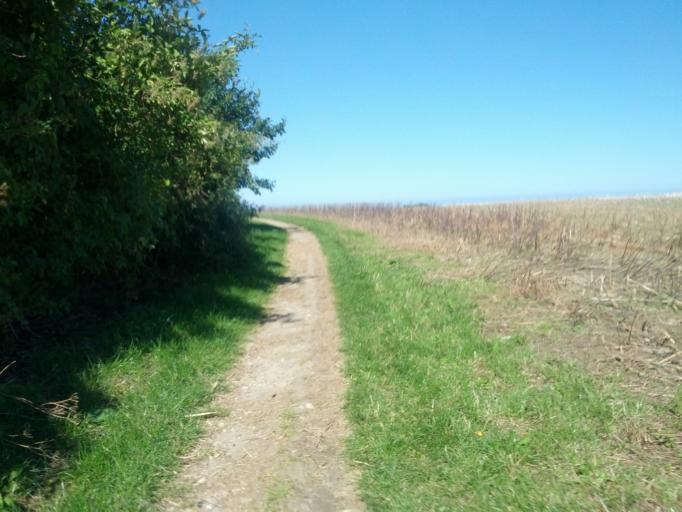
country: DE
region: Mecklenburg-Vorpommern
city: Bastorf
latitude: 54.1296
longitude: 11.6910
